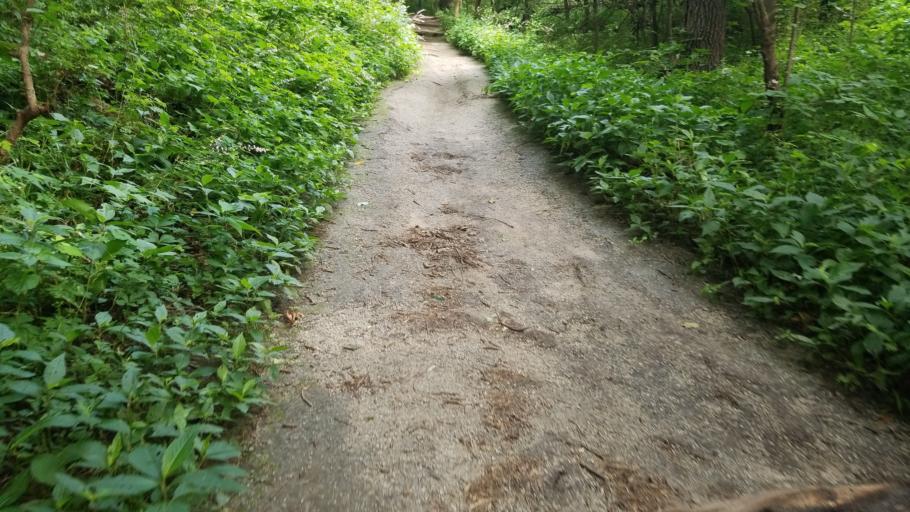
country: US
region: Nebraska
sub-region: Cass County
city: Louisville
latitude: 41.0227
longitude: -96.2486
